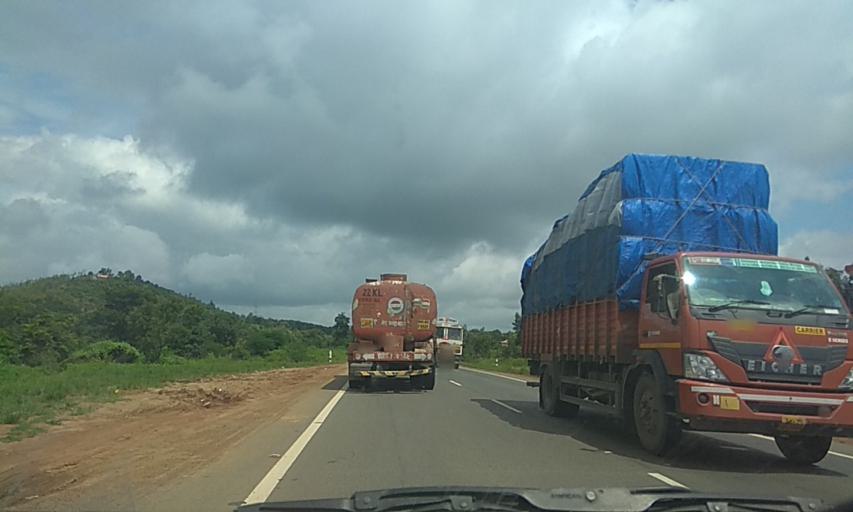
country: IN
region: Karnataka
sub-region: Dharwad
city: Hubli
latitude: 15.4214
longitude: 74.9721
